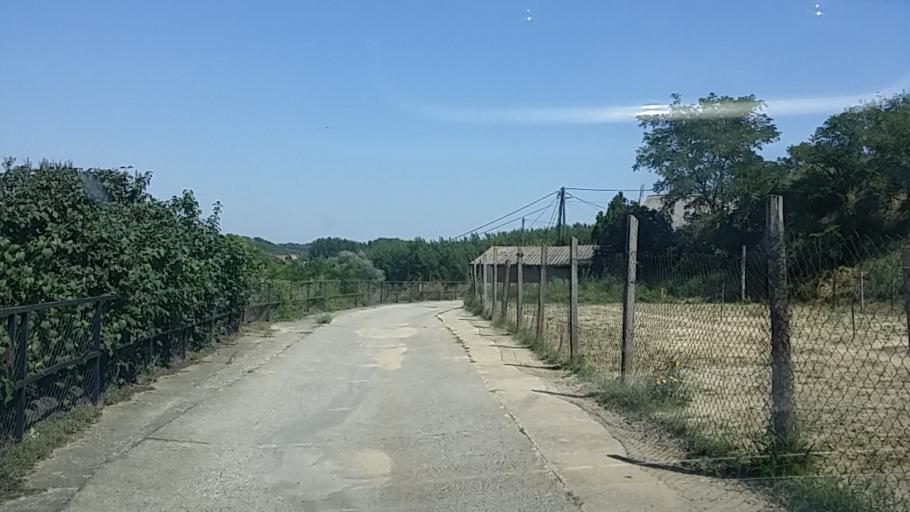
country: HU
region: Tolna
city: Paks
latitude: 46.6578
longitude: 18.8809
